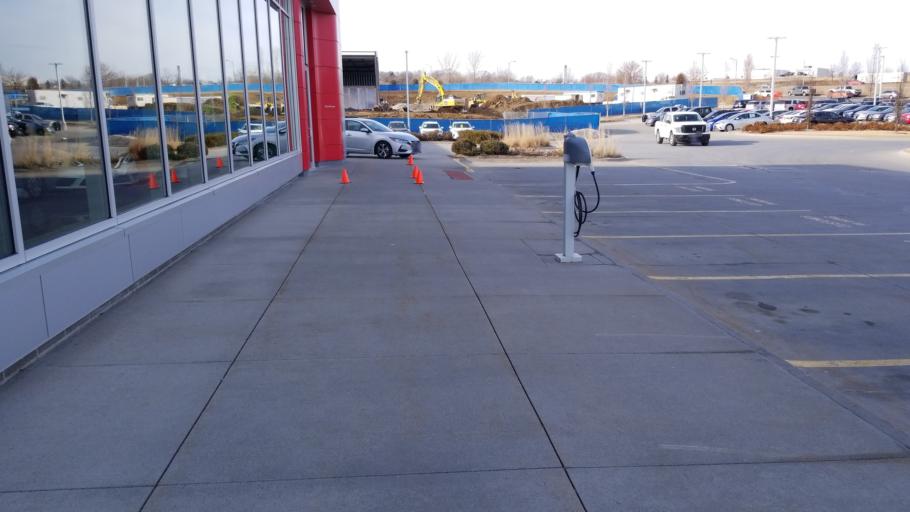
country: US
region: Nebraska
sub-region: Sarpy County
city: Offutt Air Force Base
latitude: 41.1826
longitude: -95.9355
